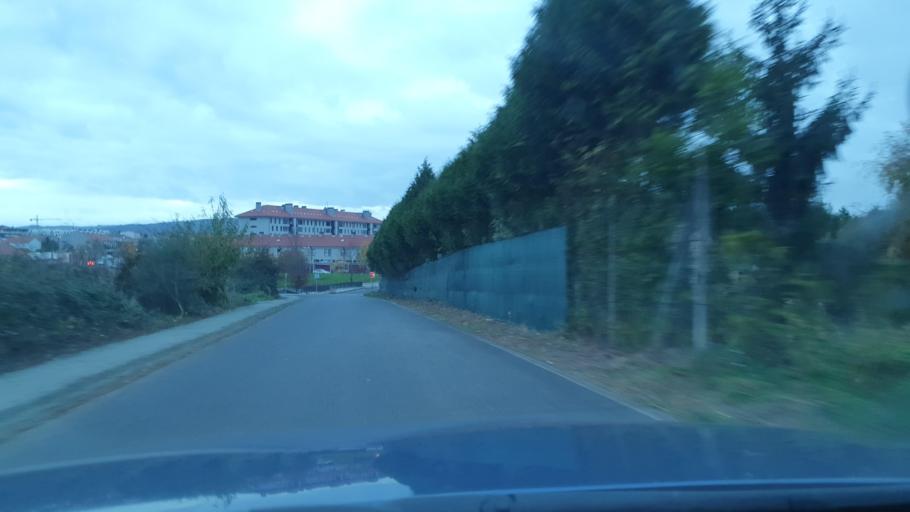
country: ES
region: Galicia
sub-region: Provincia da Coruna
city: Santiago de Compostela
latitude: 42.8548
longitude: -8.5359
